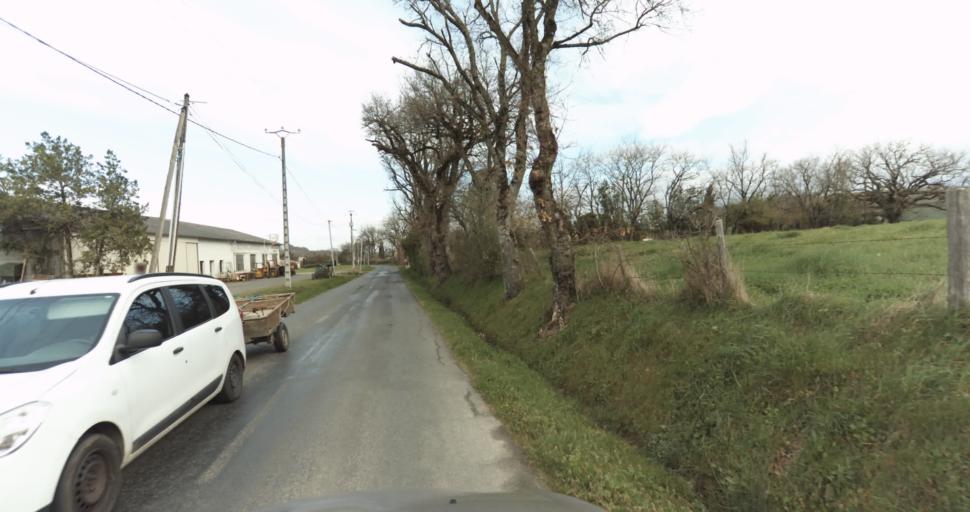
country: FR
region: Midi-Pyrenees
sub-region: Departement du Tarn
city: Puygouzon
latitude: 43.8896
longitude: 2.1928
